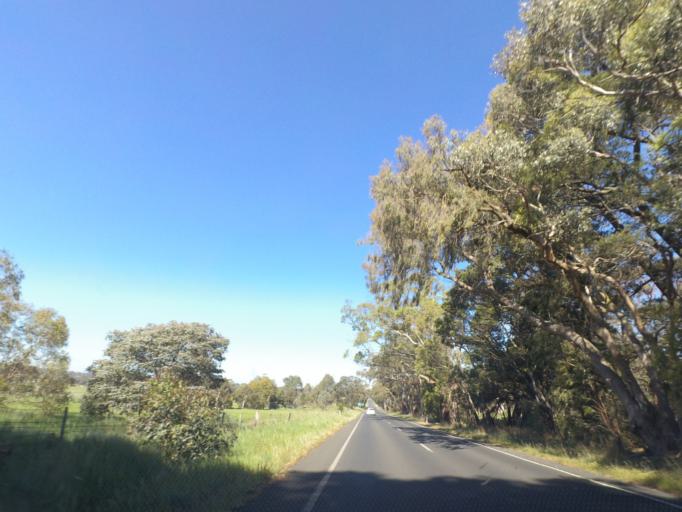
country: AU
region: Victoria
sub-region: Whittlesea
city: Whittlesea
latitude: -37.3256
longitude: 144.9625
